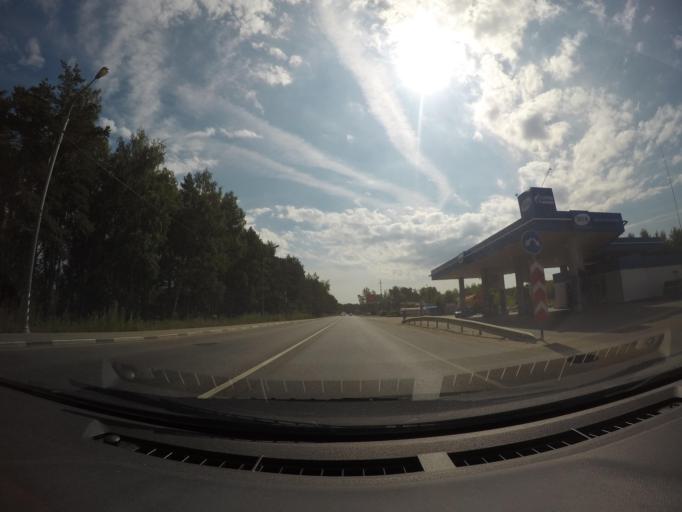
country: RU
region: Moskovskaya
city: Il'inskiy
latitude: 55.6540
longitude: 38.1163
